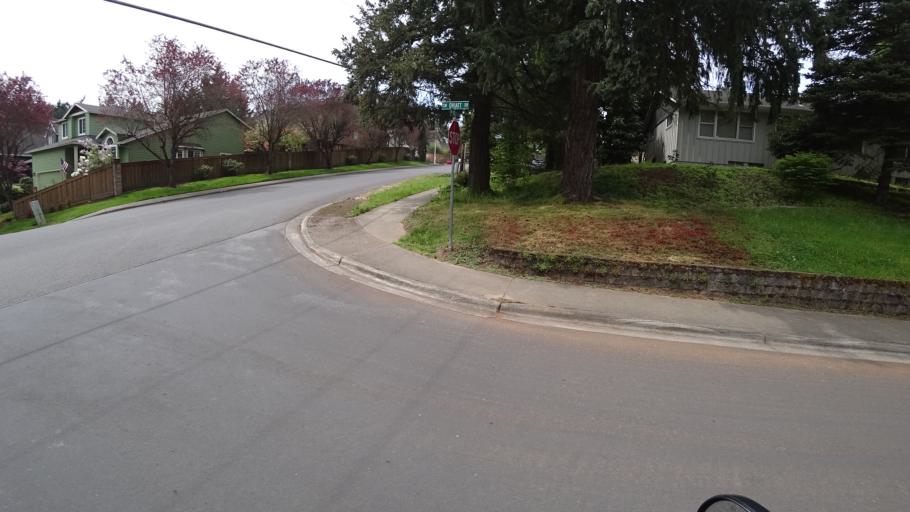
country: US
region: Oregon
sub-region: Washington County
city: Aloha
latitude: 45.4622
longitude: -122.8600
